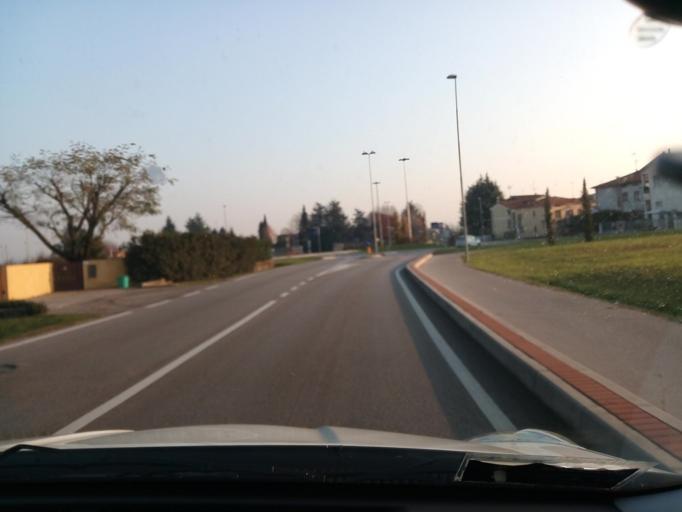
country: IT
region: Veneto
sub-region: Provincia di Vicenza
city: Schio
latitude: 45.7029
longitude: 11.3643
